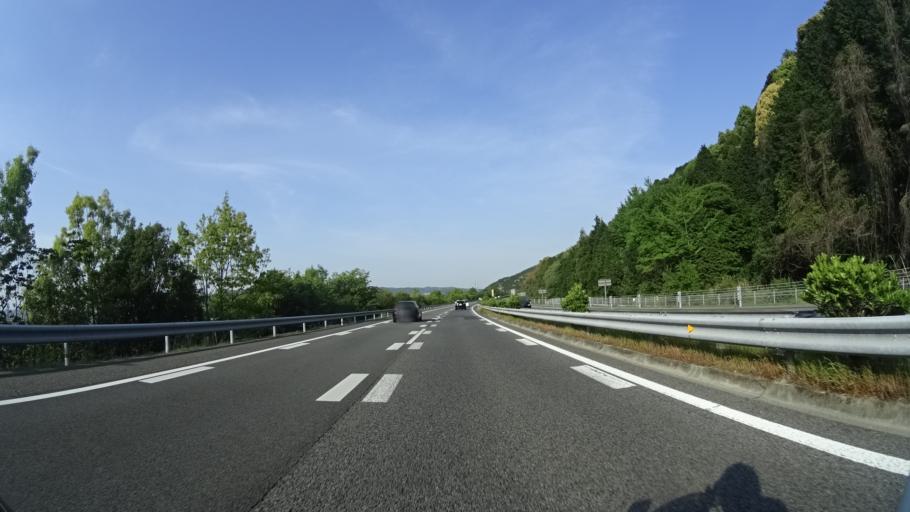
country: JP
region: Ehime
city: Saijo
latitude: 33.9043
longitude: 133.2041
